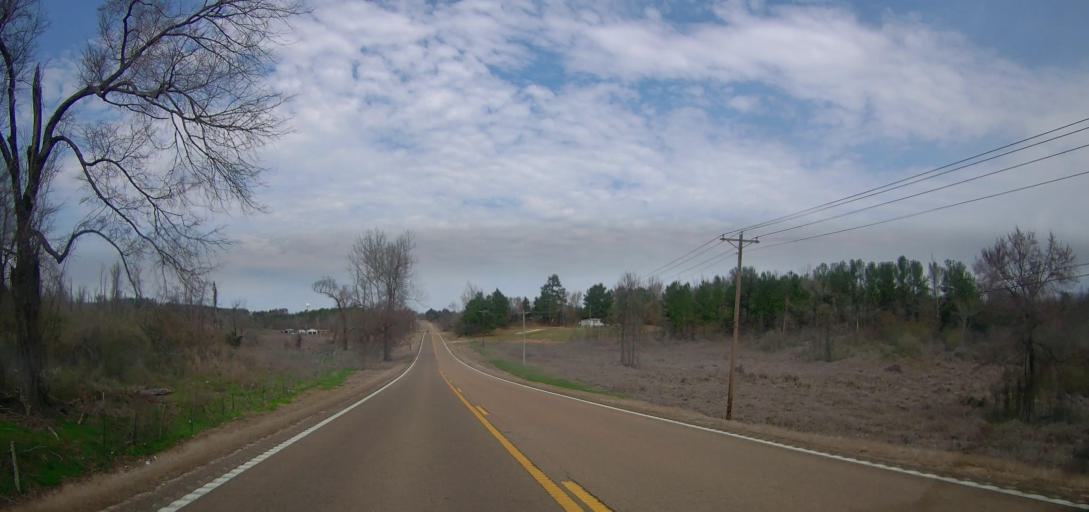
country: US
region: Mississippi
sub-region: Marshall County
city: Holly Springs
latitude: 34.7412
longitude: -89.4251
